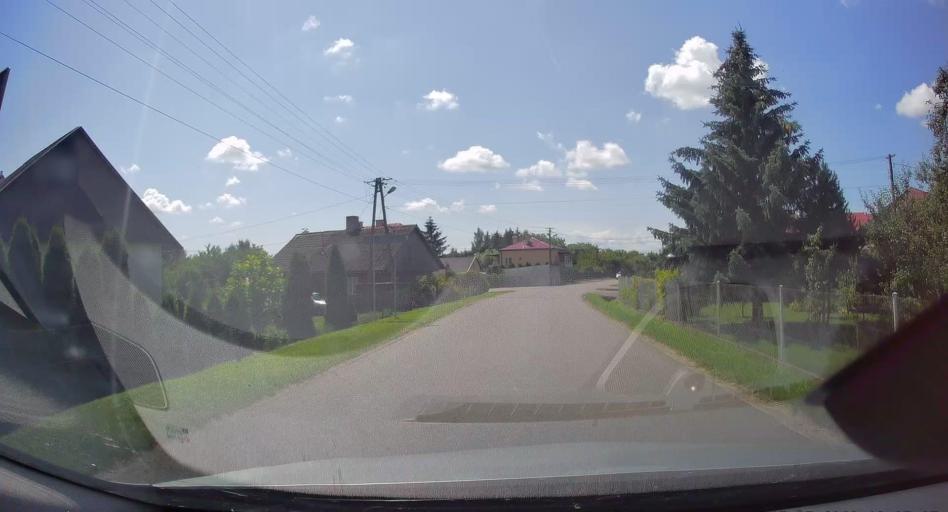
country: PL
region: Subcarpathian Voivodeship
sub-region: Powiat przemyski
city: Medyka
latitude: 49.8219
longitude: 22.8662
